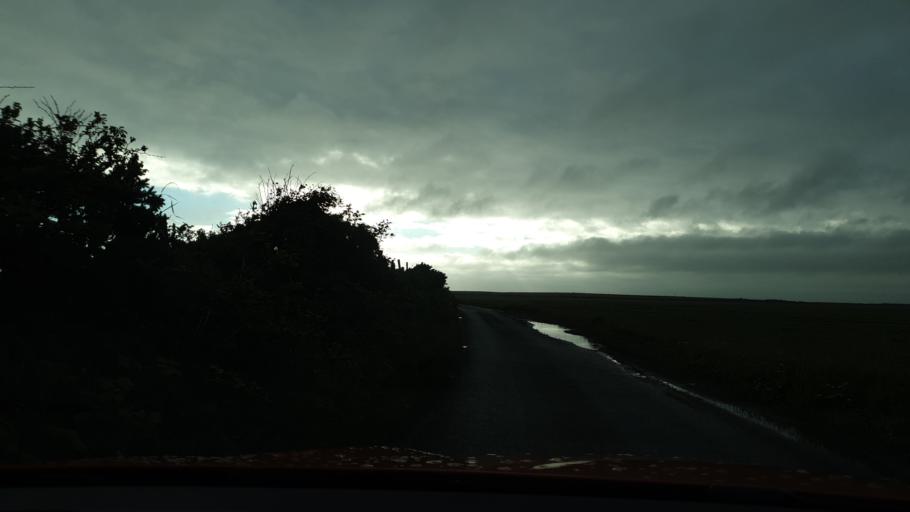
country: GB
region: England
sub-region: Cumbria
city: Barrow in Furness
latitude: 54.0661
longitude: -3.2133
